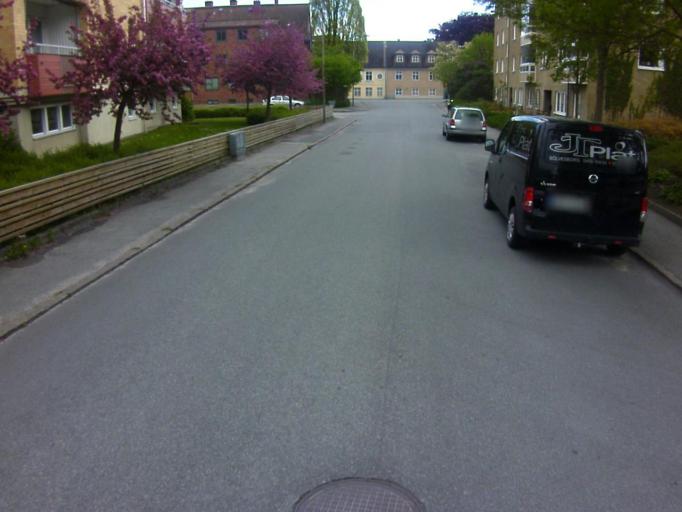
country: SE
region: Blekinge
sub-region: Solvesborgs Kommun
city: Soelvesborg
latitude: 56.0532
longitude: 14.5803
